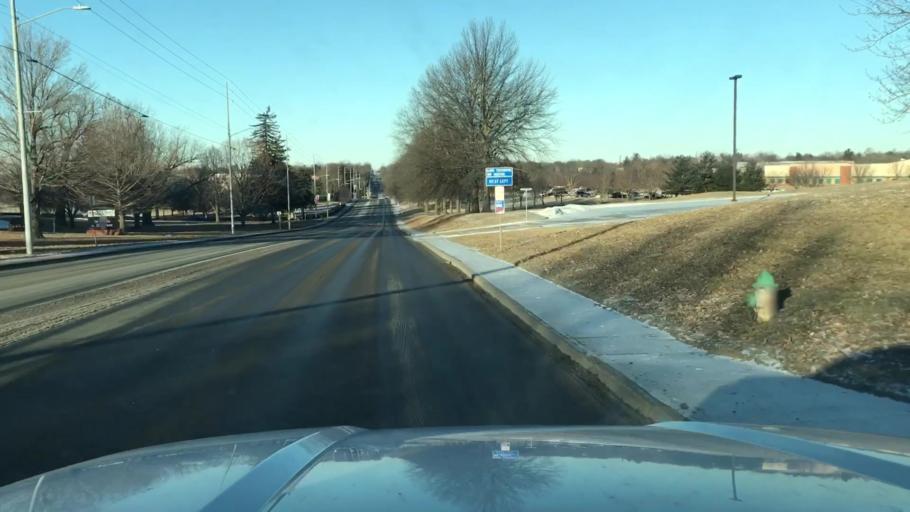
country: US
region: Missouri
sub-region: Buchanan County
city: Saint Joseph
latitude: 39.7770
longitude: -94.8076
